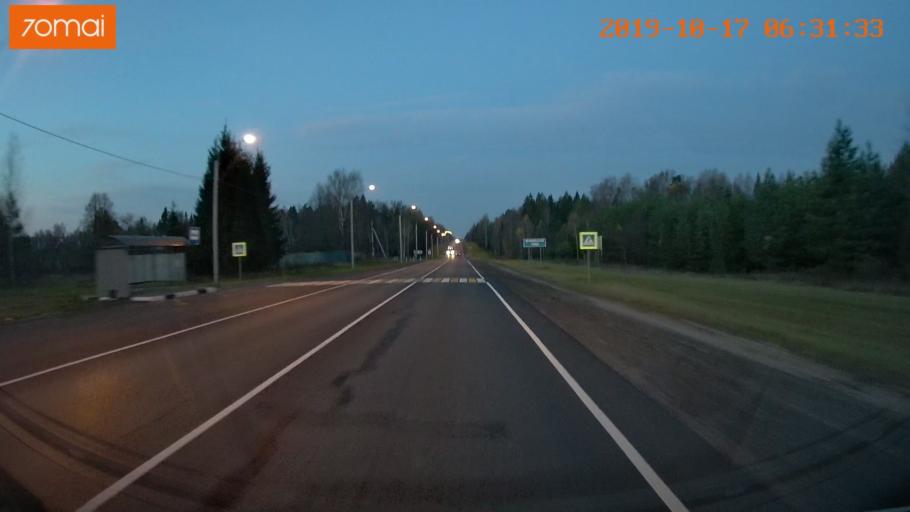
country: RU
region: Ivanovo
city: Novoye Leushino
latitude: 56.7267
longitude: 40.6951
